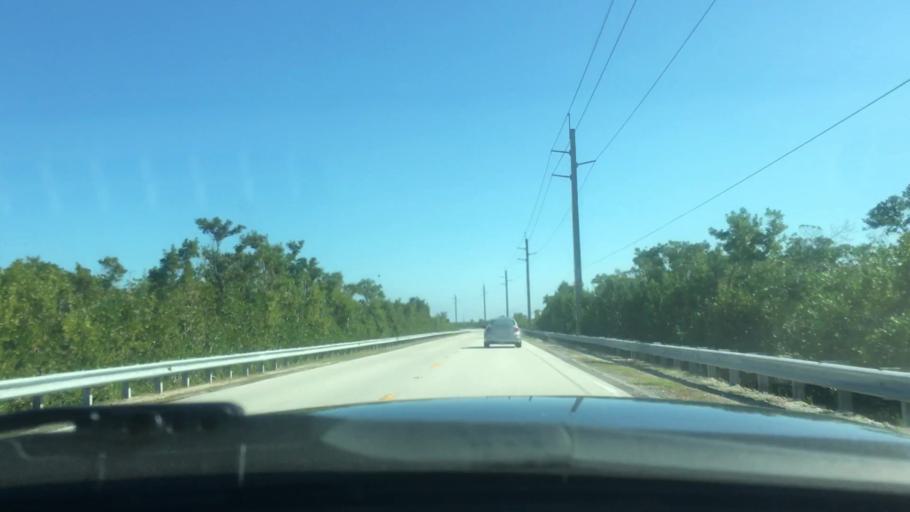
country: US
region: Florida
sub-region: Monroe County
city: North Key Largo
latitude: 25.2840
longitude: -80.3155
